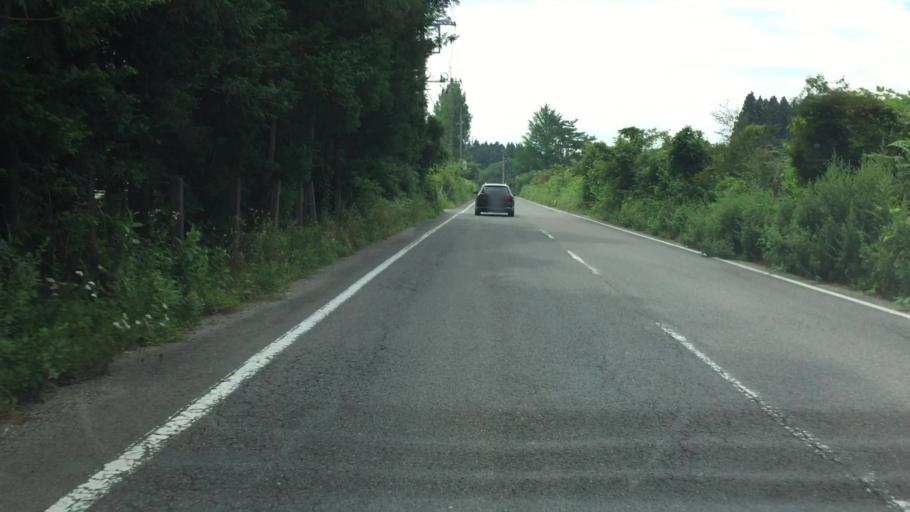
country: JP
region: Tochigi
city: Kuroiso
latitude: 37.0449
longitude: 140.0429
